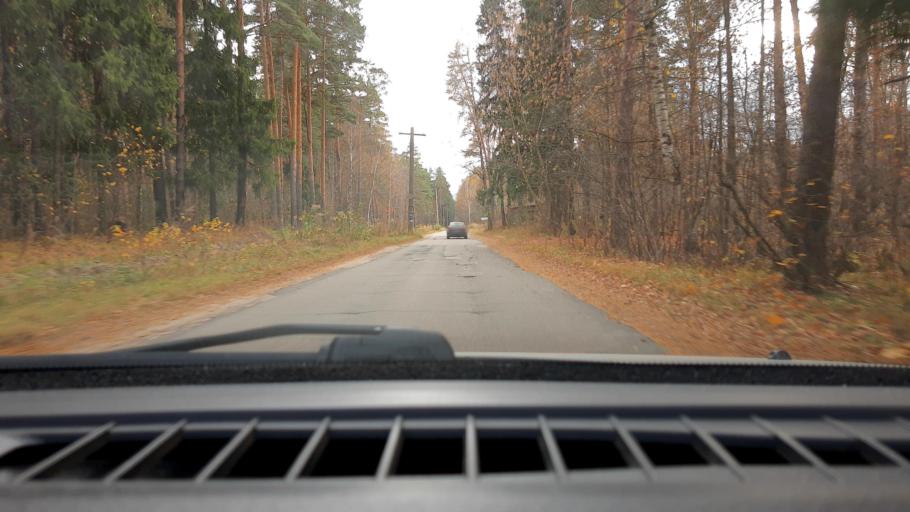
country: RU
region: Nizjnij Novgorod
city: Afonino
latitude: 56.1723
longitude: 44.0974
